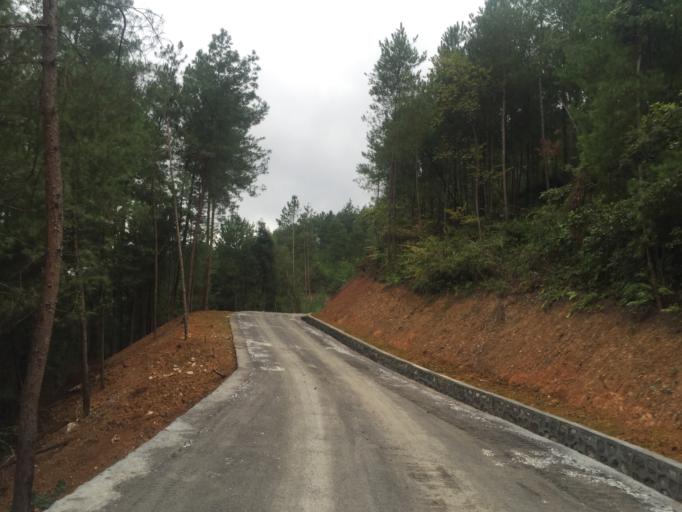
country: CN
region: Guizhou Sheng
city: Zhongba
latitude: 27.9730
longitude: 108.2208
